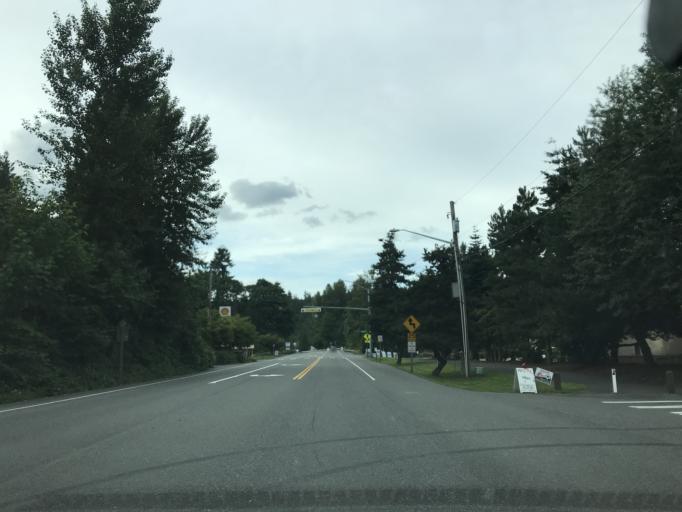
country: US
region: Washington
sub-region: King County
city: Fall City
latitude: 47.5248
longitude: -121.9364
